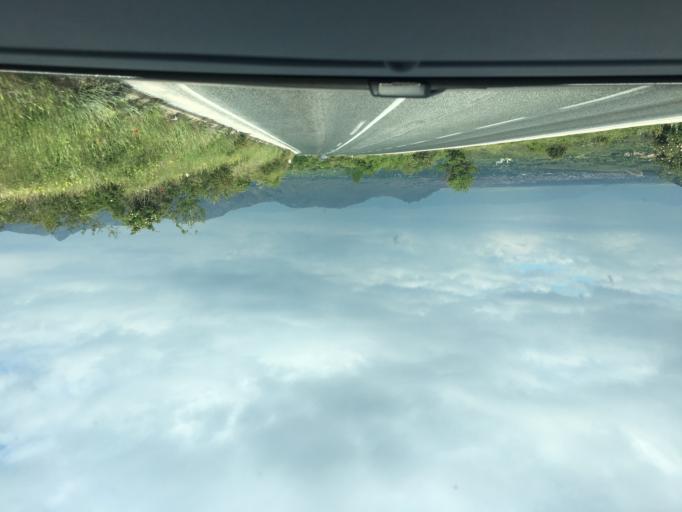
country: MK
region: Prilep
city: Prilep
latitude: 41.3689
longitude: 21.6375
